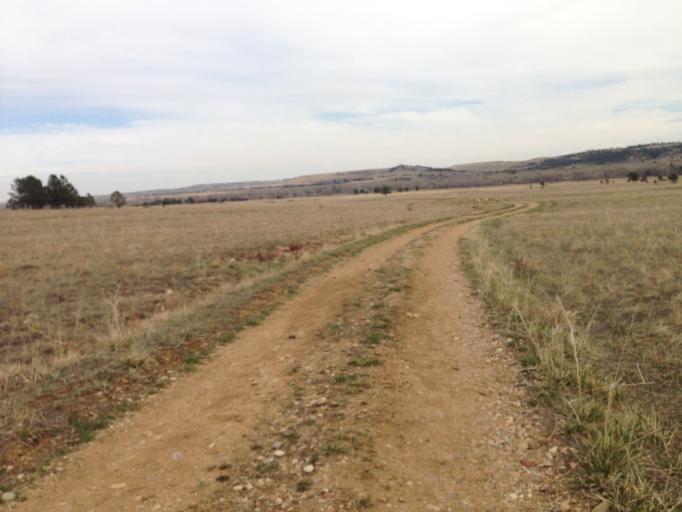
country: US
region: Colorado
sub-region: Boulder County
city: Boulder
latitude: 39.9560
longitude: -105.2562
